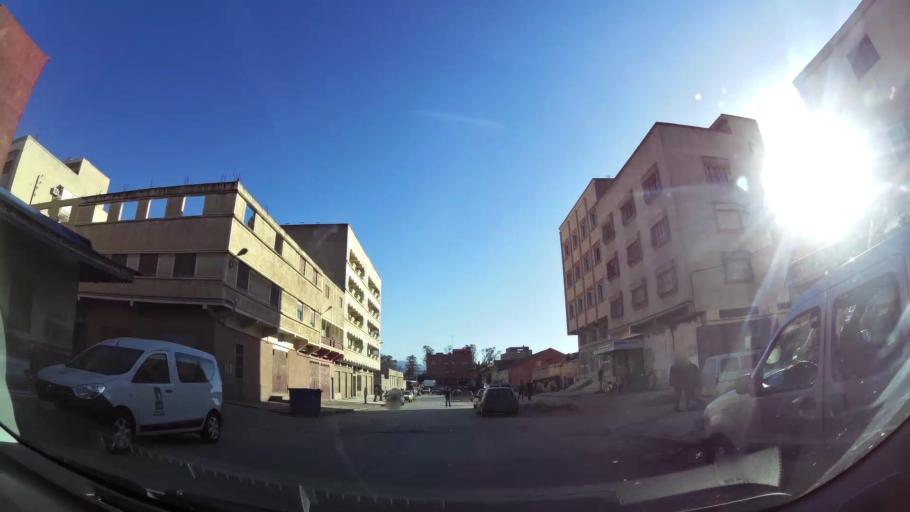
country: MA
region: Oriental
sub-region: Berkane-Taourirt
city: Berkane
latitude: 34.9254
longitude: -2.3364
